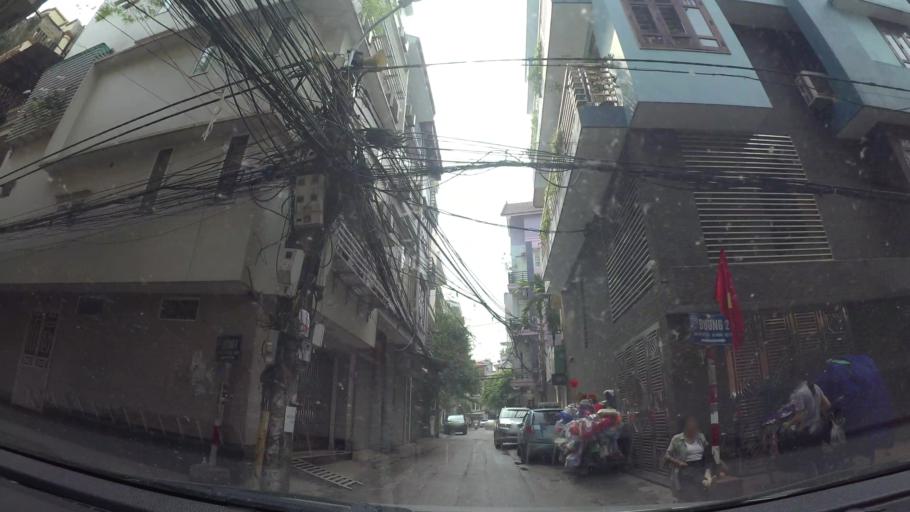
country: VN
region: Ha Noi
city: Hoan Kiem
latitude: 21.0503
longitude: 105.8433
